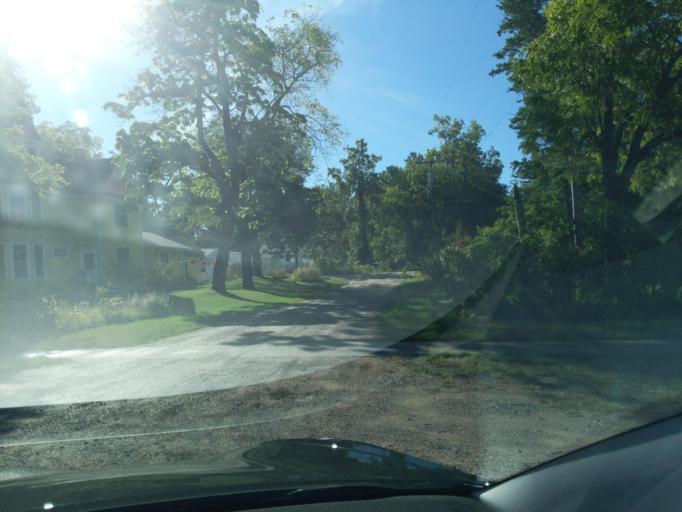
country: US
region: Michigan
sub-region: Antrim County
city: Elk Rapids
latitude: 44.8948
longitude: -85.4210
